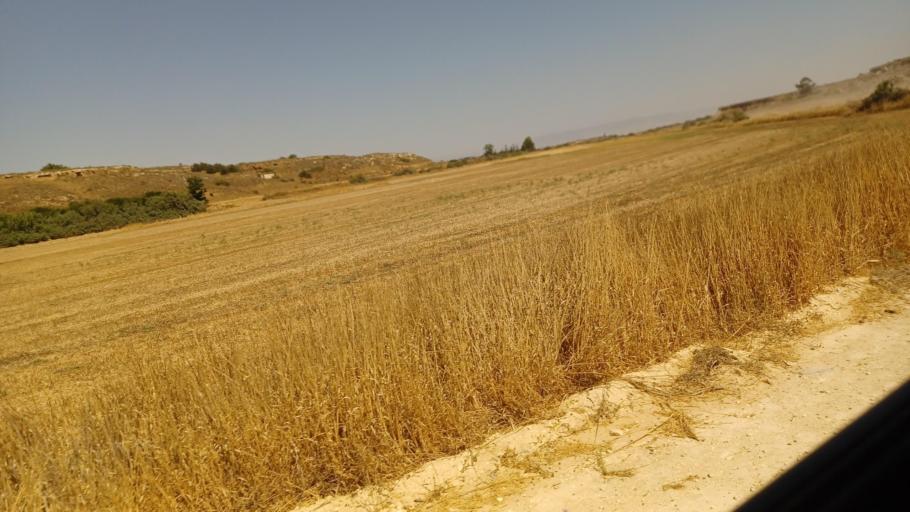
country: CY
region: Ammochostos
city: Acheritou
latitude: 35.0970
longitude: 33.8753
